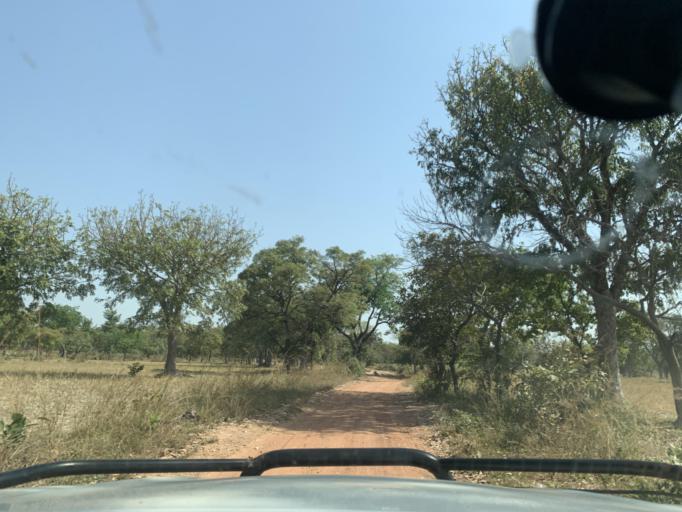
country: ML
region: Sikasso
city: Kolondieba
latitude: 10.8925
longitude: -6.7505
